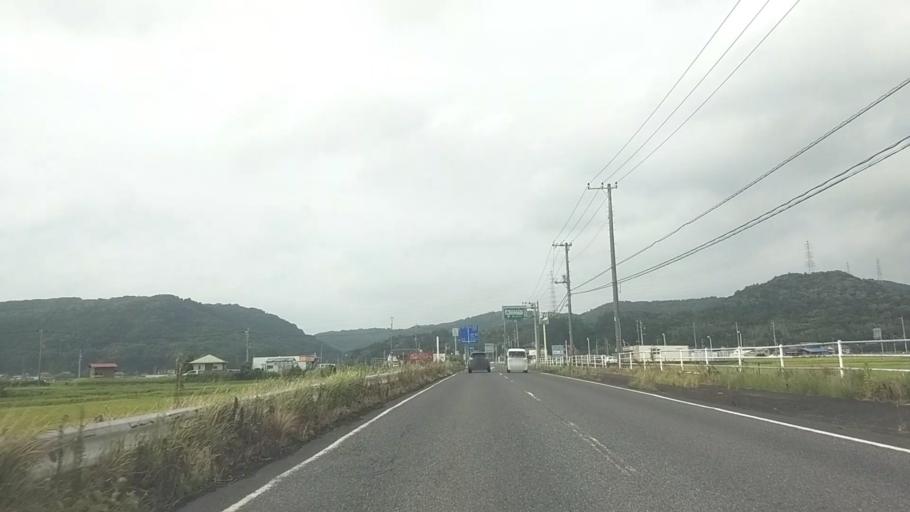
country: JP
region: Chiba
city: Kisarazu
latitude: 35.3005
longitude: 139.9869
